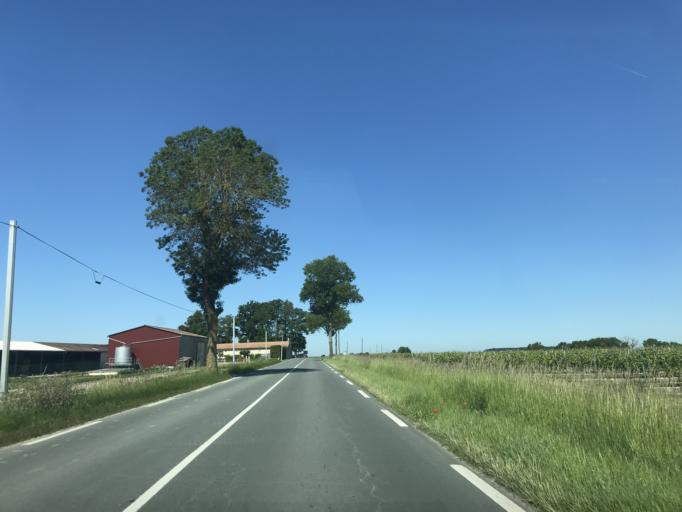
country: FR
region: Poitou-Charentes
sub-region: Departement de la Charente-Maritime
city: Perignac
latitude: 45.5735
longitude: -0.4212
